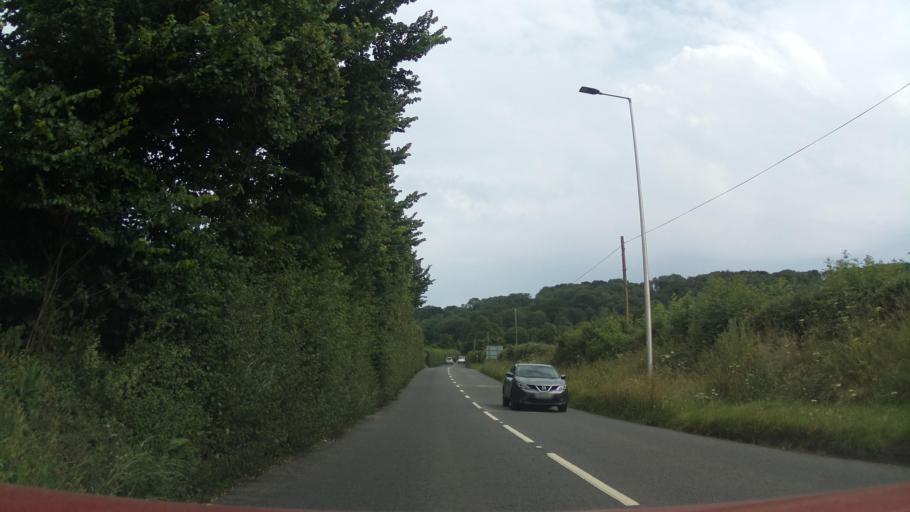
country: GB
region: England
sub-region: Devon
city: Sidmouth
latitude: 50.7014
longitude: -3.2185
